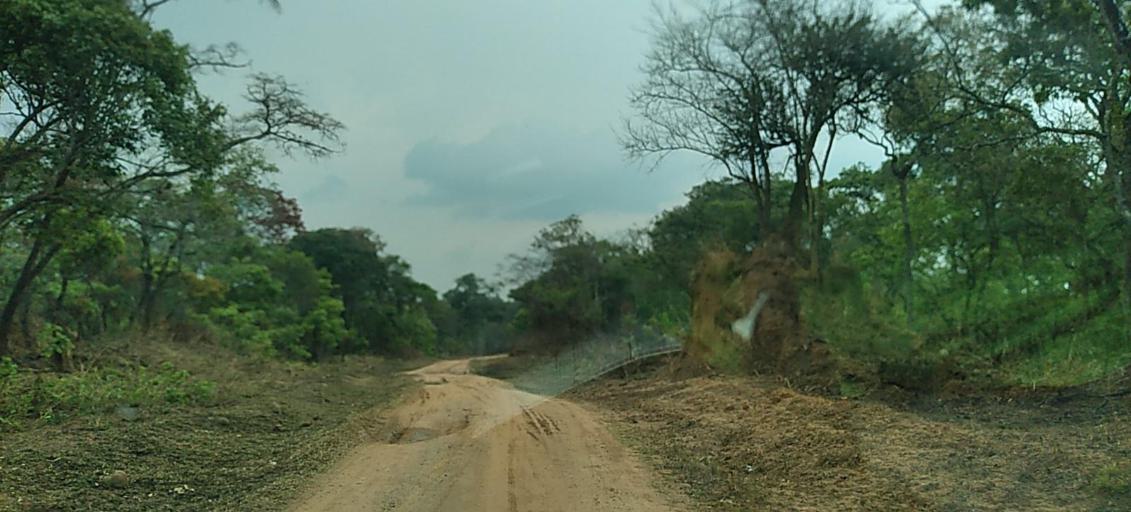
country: ZM
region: North-Western
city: Mwinilunga
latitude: -11.4697
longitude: 24.4627
